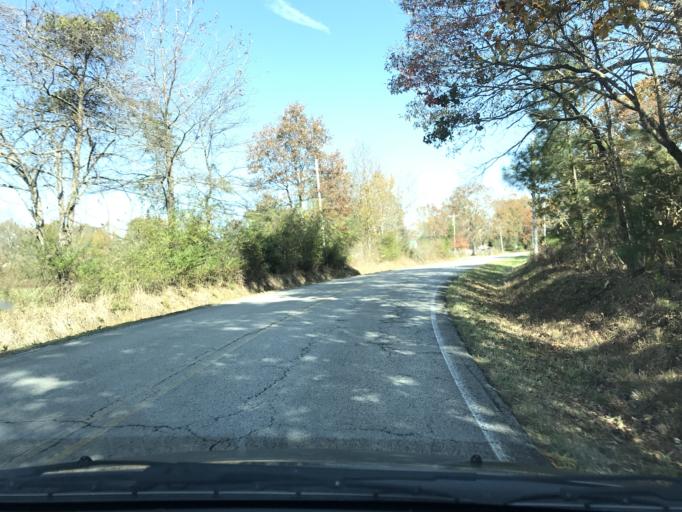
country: US
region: Tennessee
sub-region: Coffee County
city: Tullahoma
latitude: 35.3969
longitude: -86.1637
